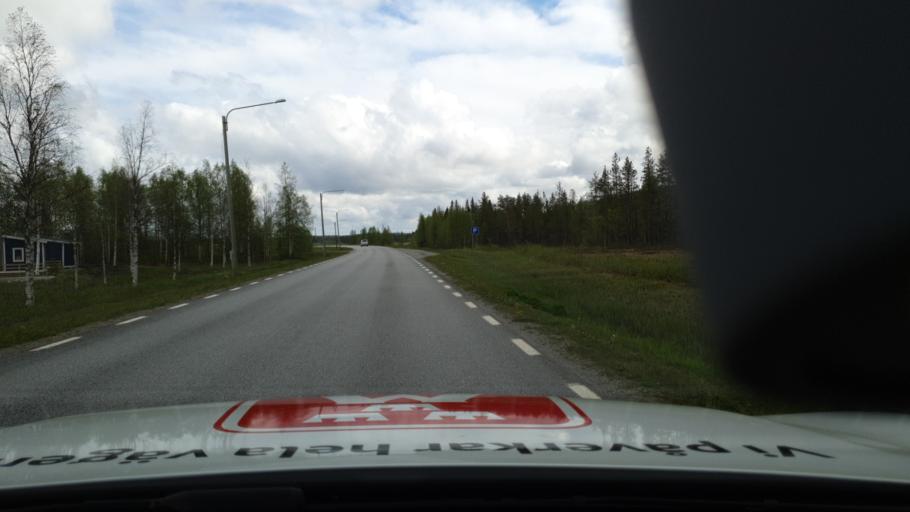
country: SE
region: Vaesterbotten
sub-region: Vilhelmina Kommun
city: Sjoberg
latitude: 64.6334
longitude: 16.3777
